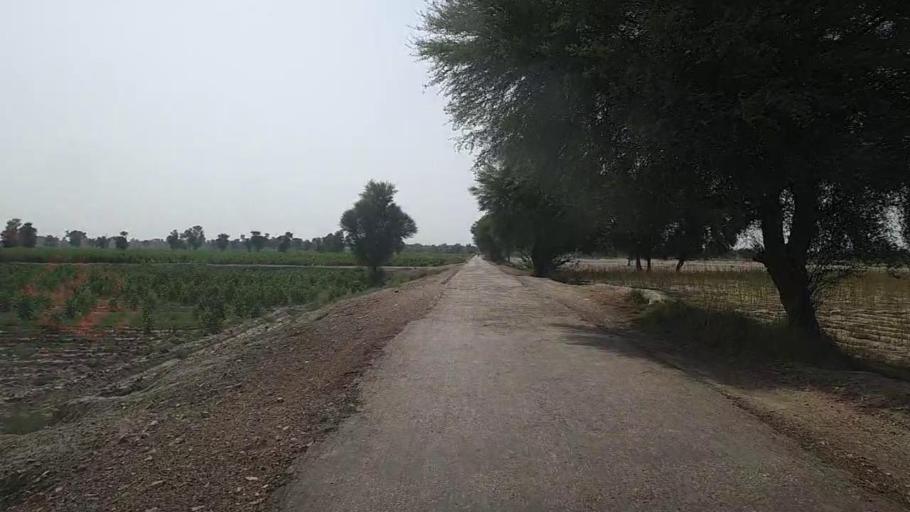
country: PK
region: Sindh
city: Pad Idan
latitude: 26.7698
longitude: 68.3133
